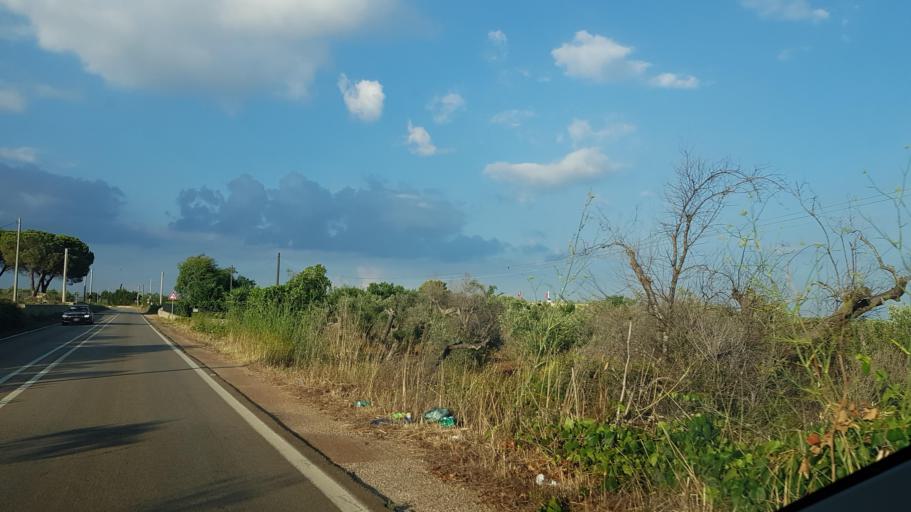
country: IT
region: Apulia
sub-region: Provincia di Lecce
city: Acquarica del Capo
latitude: 39.8675
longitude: 18.2168
